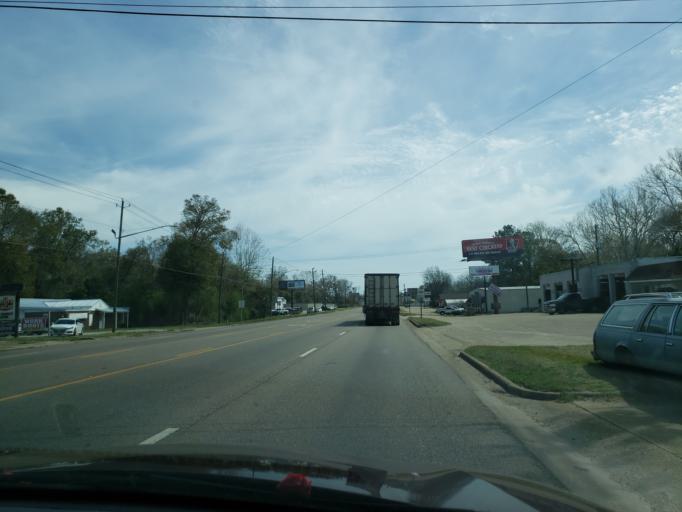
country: US
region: Alabama
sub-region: Dallas County
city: Selma
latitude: 32.4323
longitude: -87.0427
